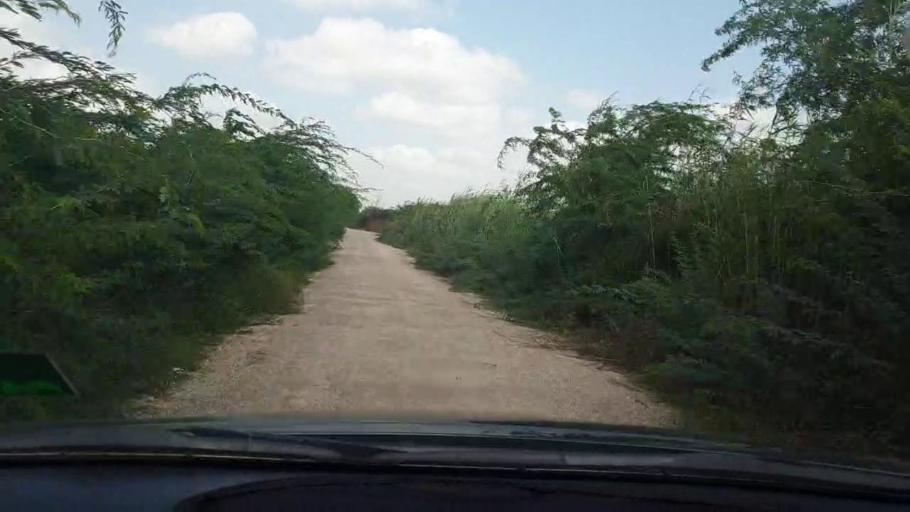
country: PK
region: Sindh
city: Tando Bago
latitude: 24.8538
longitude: 69.0342
